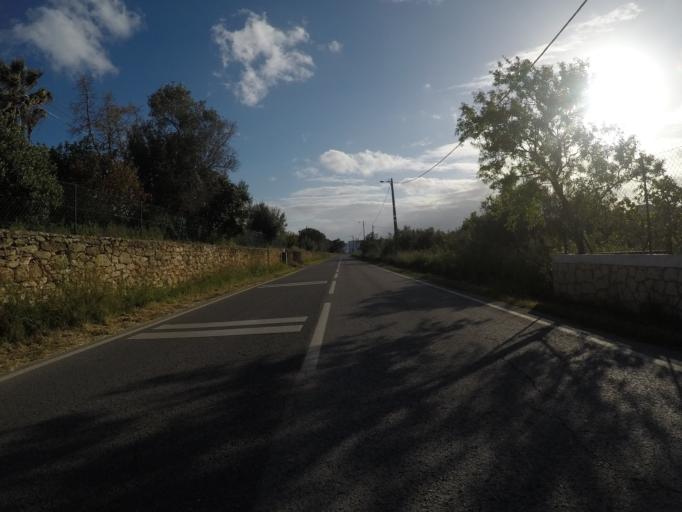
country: PT
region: Faro
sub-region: Lagoa
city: Carvoeiro
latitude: 37.1120
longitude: -8.4536
